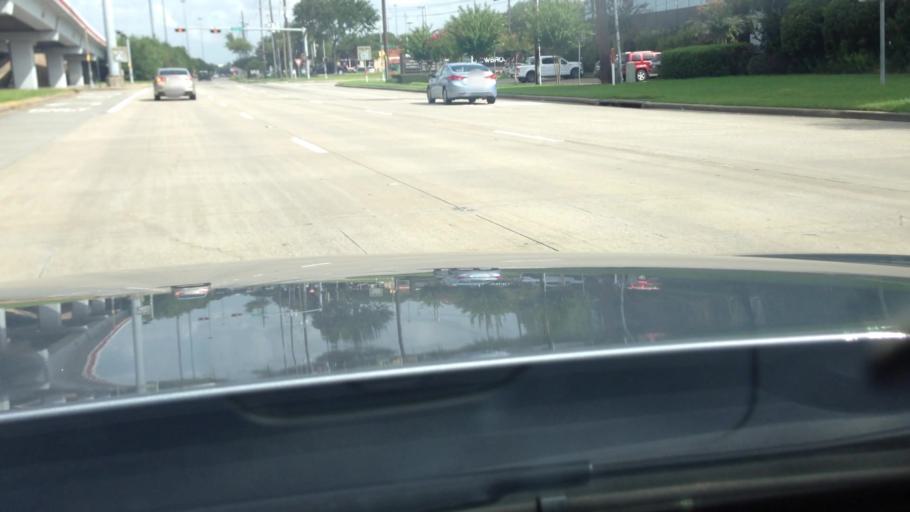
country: US
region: Texas
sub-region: Harris County
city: Hudson
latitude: 29.9564
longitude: -95.5415
